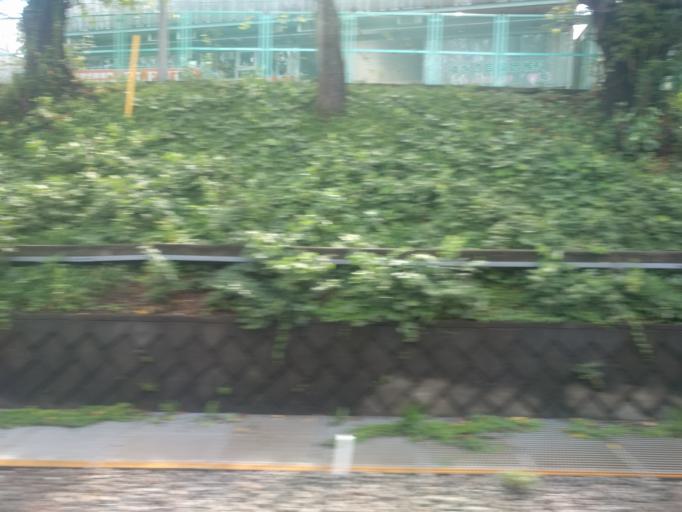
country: JP
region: Tokyo
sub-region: Machida-shi
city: Machida
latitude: 35.5619
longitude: 139.4626
